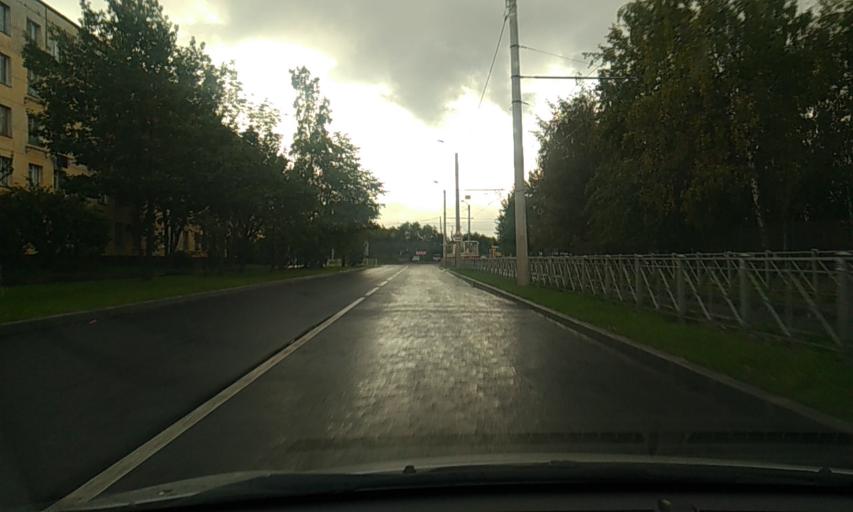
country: RU
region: St.-Petersburg
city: Sosnovaya Polyana
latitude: 59.8269
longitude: 30.1402
